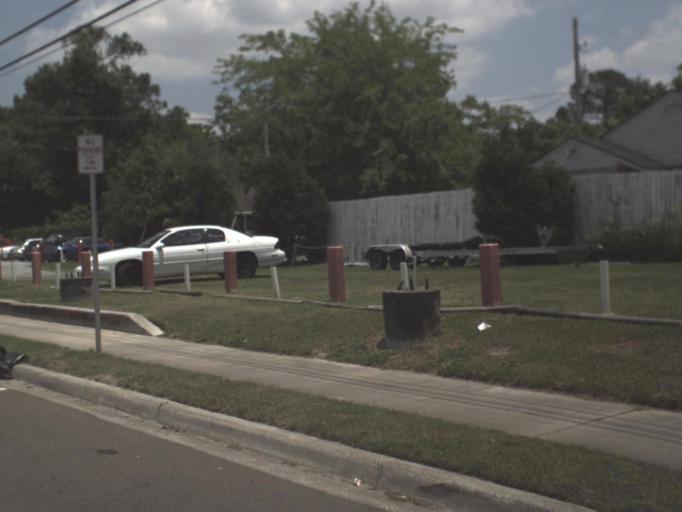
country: US
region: Florida
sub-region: Duval County
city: Jacksonville
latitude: 30.2865
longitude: -81.7303
